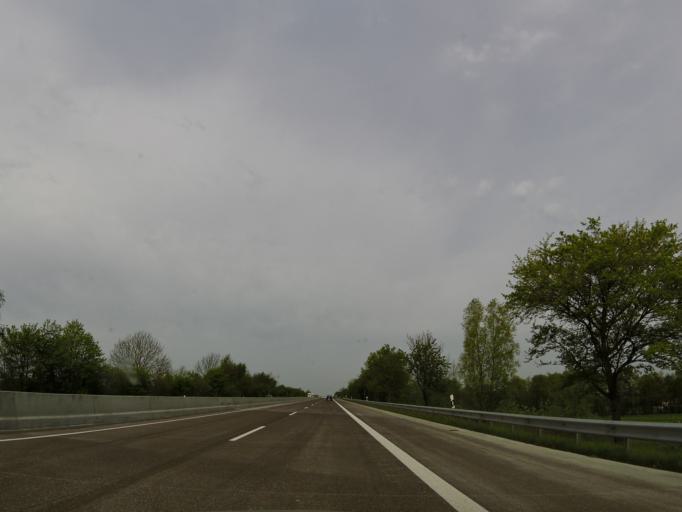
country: DE
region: Schleswig-Holstein
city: Horst
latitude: 53.8168
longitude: 9.6569
